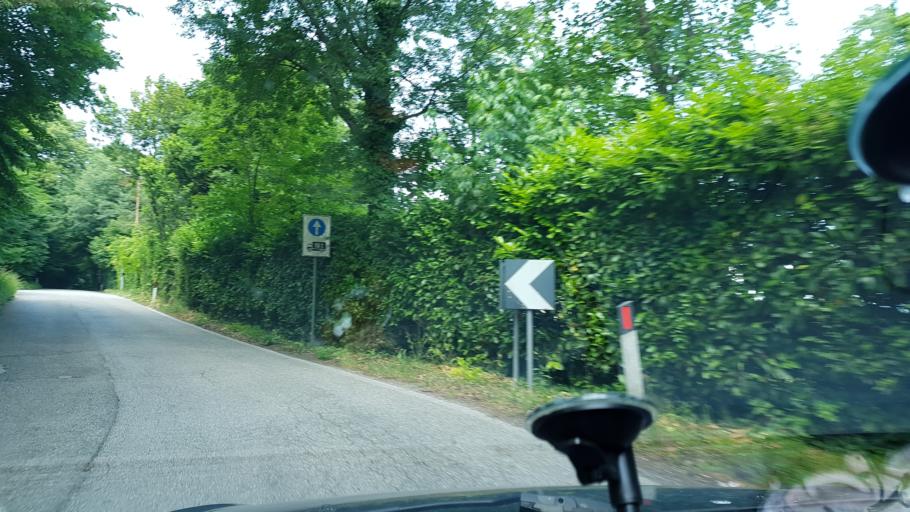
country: IT
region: Friuli Venezia Giulia
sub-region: Provincia di Gorizia
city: Savogna d'Isonzo
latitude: 45.8941
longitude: 13.5735
